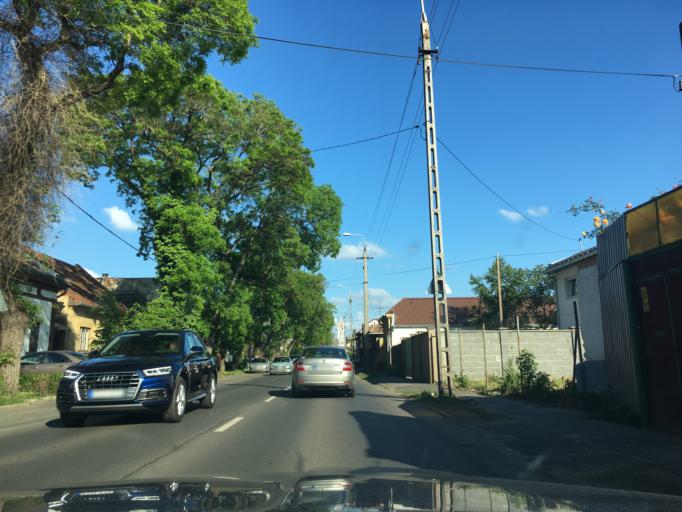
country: HU
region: Hajdu-Bihar
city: Debrecen
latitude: 47.5403
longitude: 21.6312
